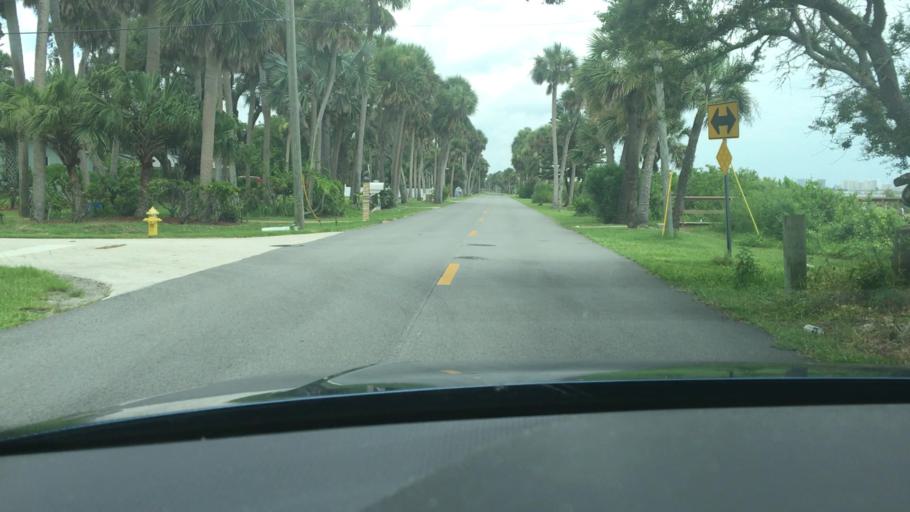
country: US
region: Florida
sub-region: Volusia County
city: Port Orange
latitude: 29.1278
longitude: -80.9777
